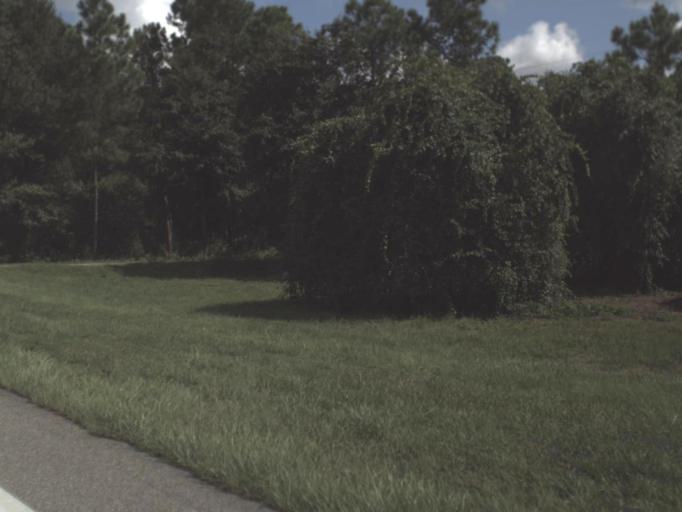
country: US
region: Florida
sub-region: Polk County
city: Polk City
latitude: 28.2072
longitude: -81.8204
